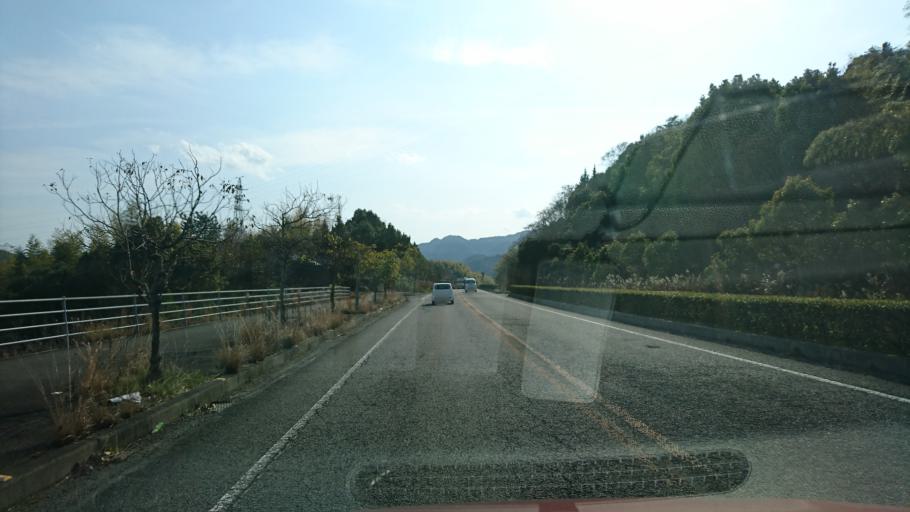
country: JP
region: Ehime
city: Saijo
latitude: 34.0122
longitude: 133.0337
